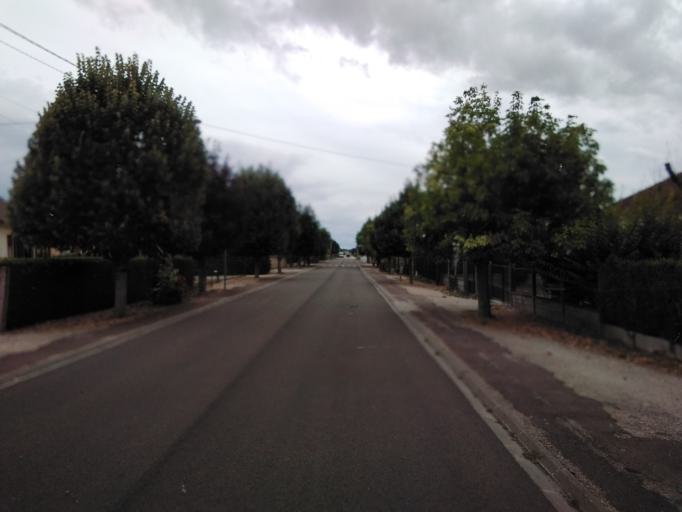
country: FR
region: Champagne-Ardenne
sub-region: Departement de l'Aube
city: Brienne-le-Chateau
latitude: 48.3866
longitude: 4.5292
